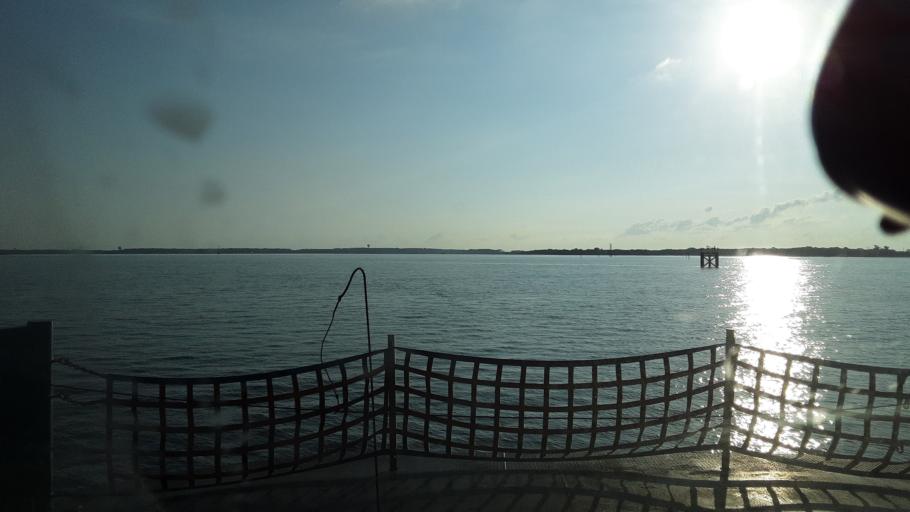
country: US
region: North Carolina
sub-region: New Hanover County
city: Kure Beach
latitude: 33.9610
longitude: -77.9520
